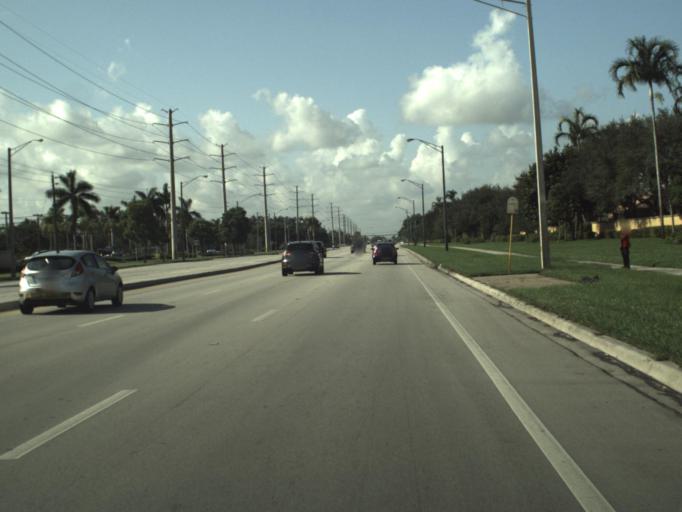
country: US
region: Florida
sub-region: Broward County
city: Parkland
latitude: 26.2931
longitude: -80.2022
